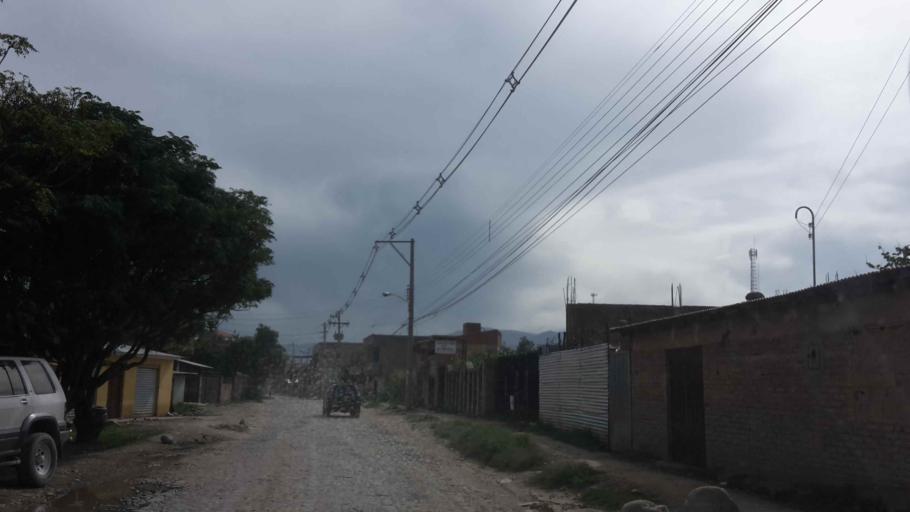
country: BO
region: Cochabamba
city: Cochabamba
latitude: -17.3364
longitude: -66.2615
